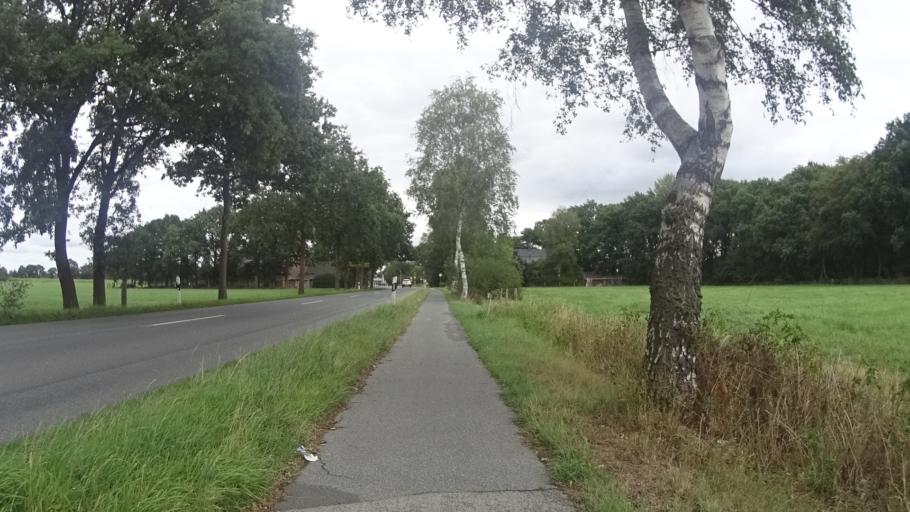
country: DE
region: Lower Saxony
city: Schiffdorf
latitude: 53.5434
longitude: 8.6810
